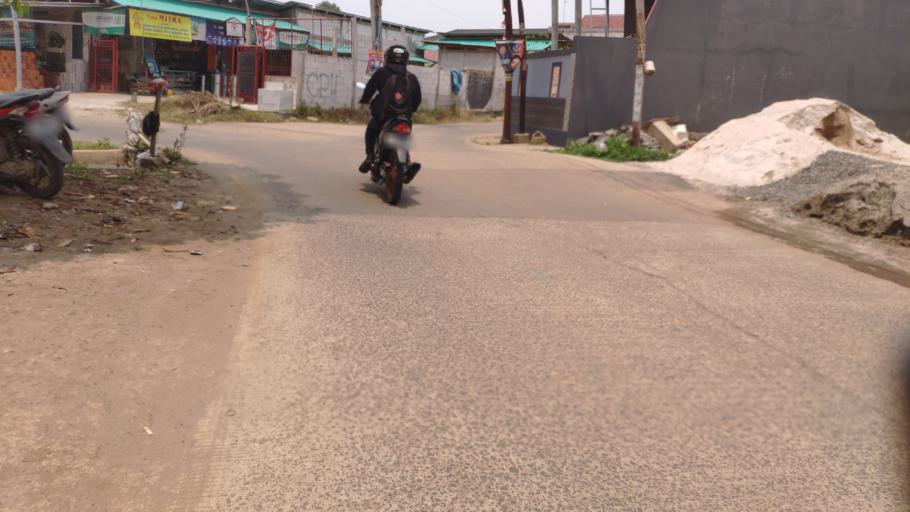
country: ID
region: West Java
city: Sawangan
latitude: -6.3839
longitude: 106.7864
